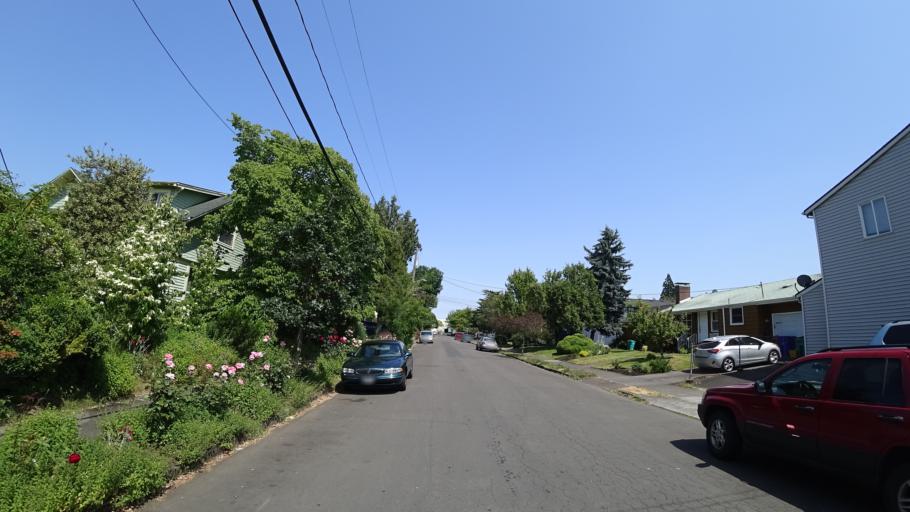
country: US
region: Oregon
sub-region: Multnomah County
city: Portland
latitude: 45.5778
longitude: -122.7026
